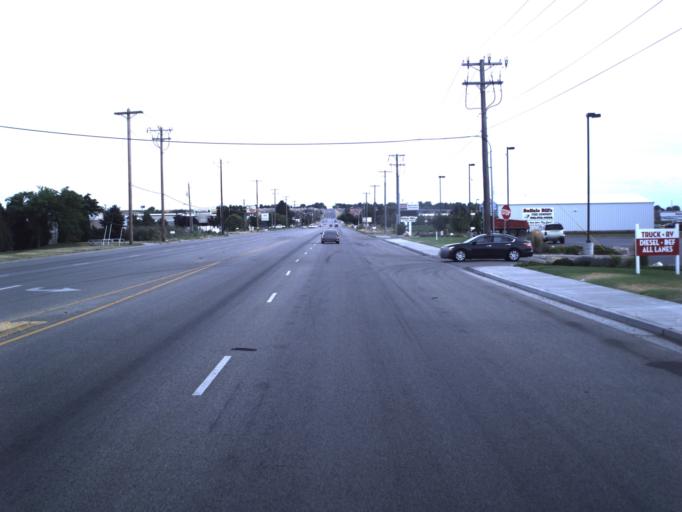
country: US
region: Utah
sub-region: Weber County
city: West Haven
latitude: 41.2191
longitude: -112.0258
